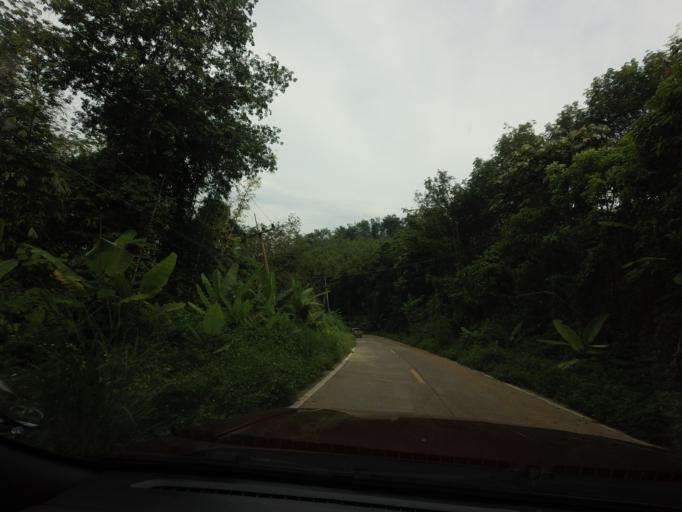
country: TH
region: Yala
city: Than To
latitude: 6.0696
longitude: 101.3528
